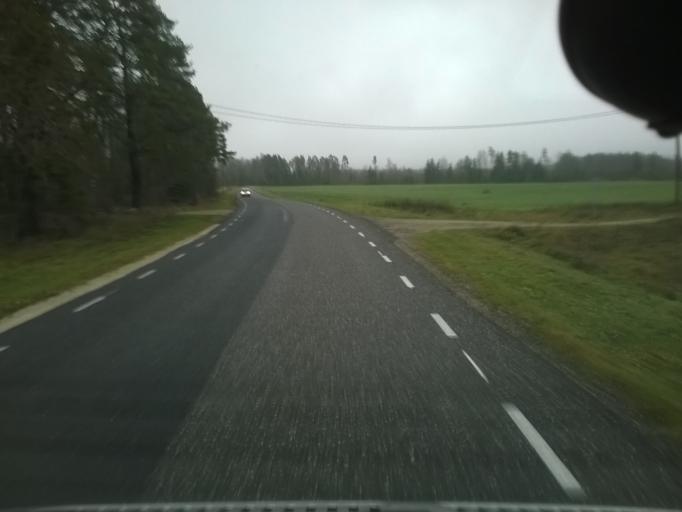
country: EE
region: Harju
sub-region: Saue linn
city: Saue
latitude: 59.1440
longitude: 24.5542
